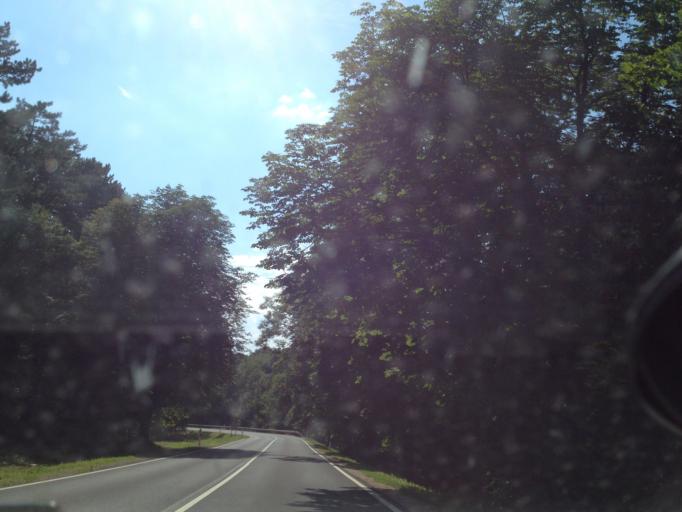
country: HU
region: Veszprem
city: Ajka
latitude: 47.2115
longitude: 17.6207
